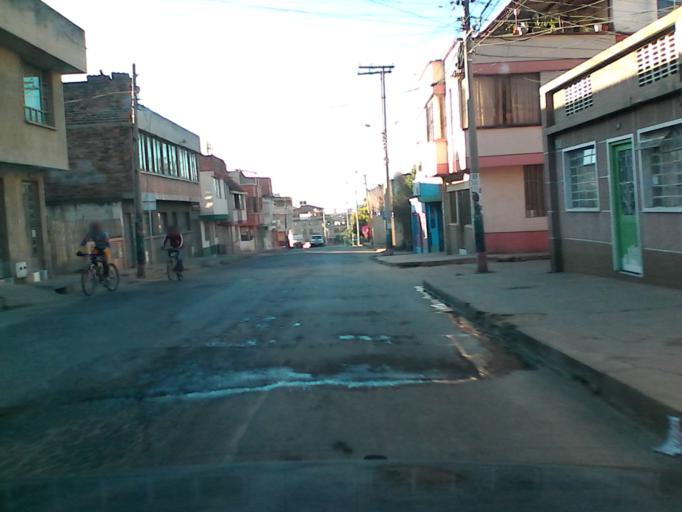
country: CO
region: Boyaca
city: Duitama
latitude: 5.8350
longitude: -73.0369
